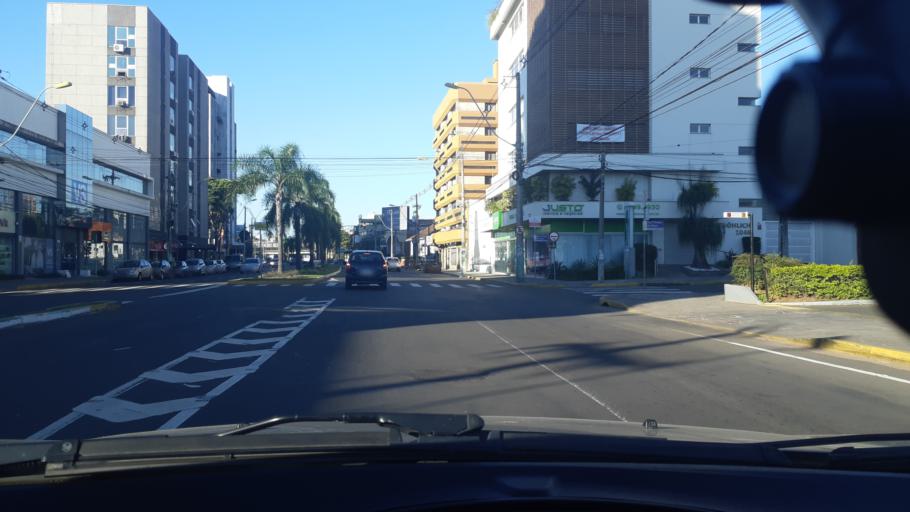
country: BR
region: Rio Grande do Sul
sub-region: Sao Leopoldo
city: Sao Leopoldo
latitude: -29.7712
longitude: -51.1458
